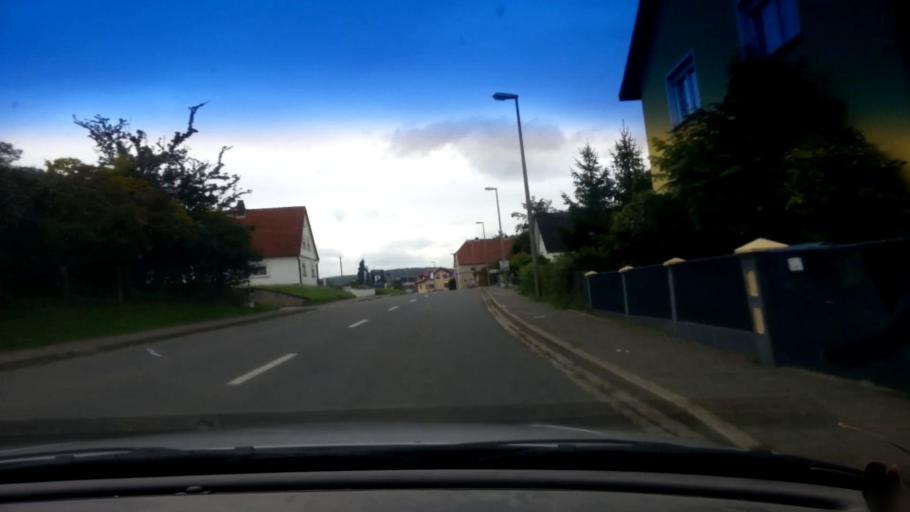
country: DE
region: Bavaria
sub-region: Upper Franconia
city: Baunach
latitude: 49.9891
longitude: 10.8471
